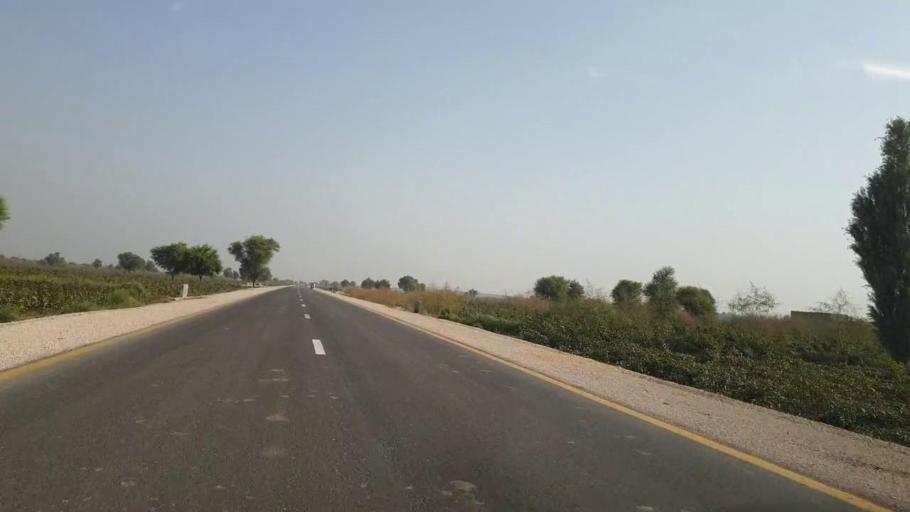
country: PK
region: Sindh
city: Sehwan
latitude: 26.4675
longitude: 67.7955
